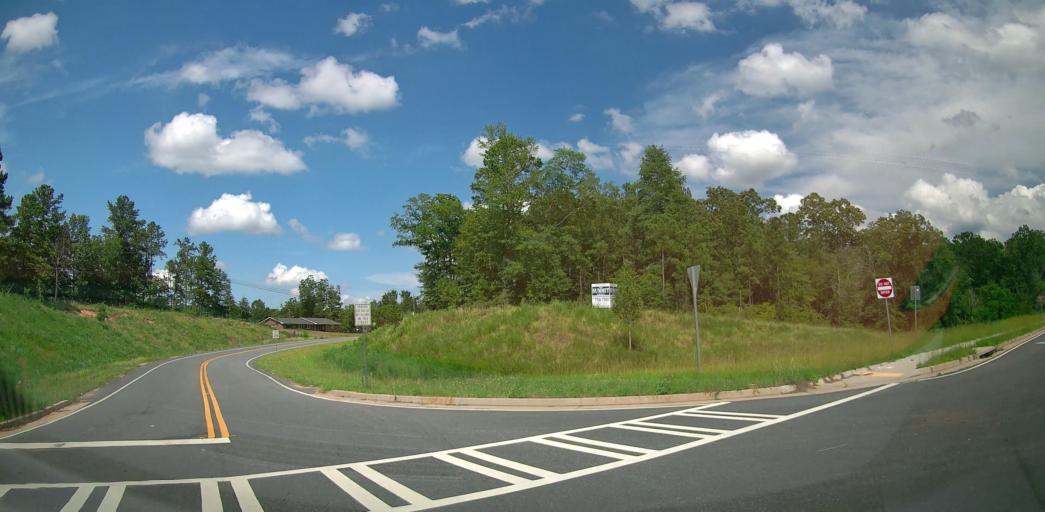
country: US
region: Georgia
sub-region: Peach County
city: Byron
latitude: 32.7164
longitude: -83.7035
